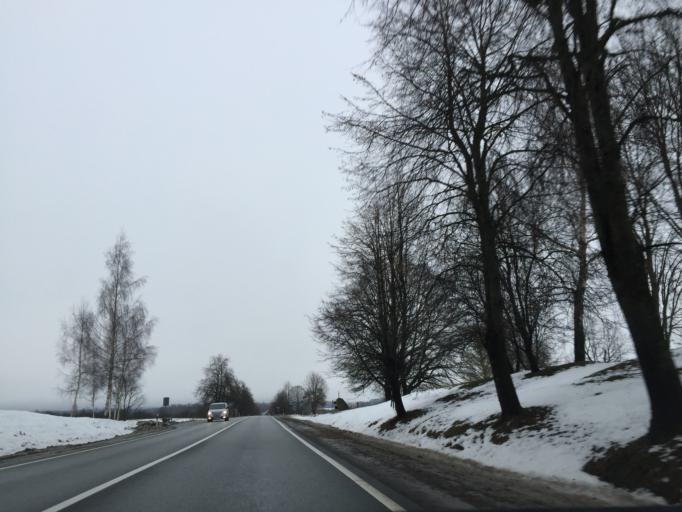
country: LV
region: Krimulda
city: Ragana
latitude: 57.1690
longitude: 24.7019
